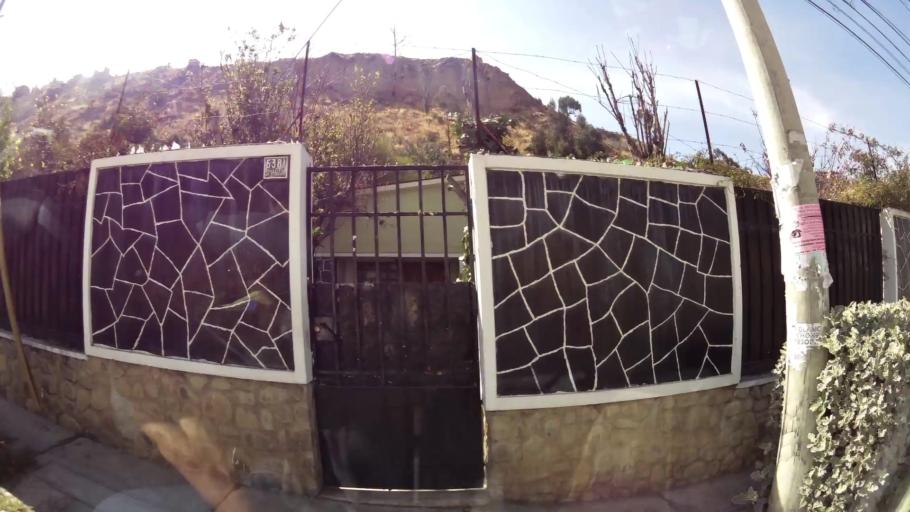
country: BO
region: La Paz
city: La Paz
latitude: -16.5205
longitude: -68.0856
